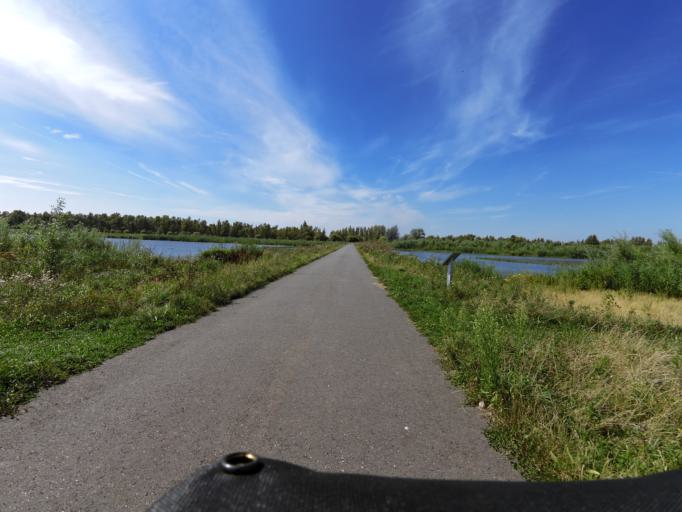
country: NL
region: South Holland
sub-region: Gemeente Sliedrecht
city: Sliedrecht
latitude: 51.7692
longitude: 4.7602
